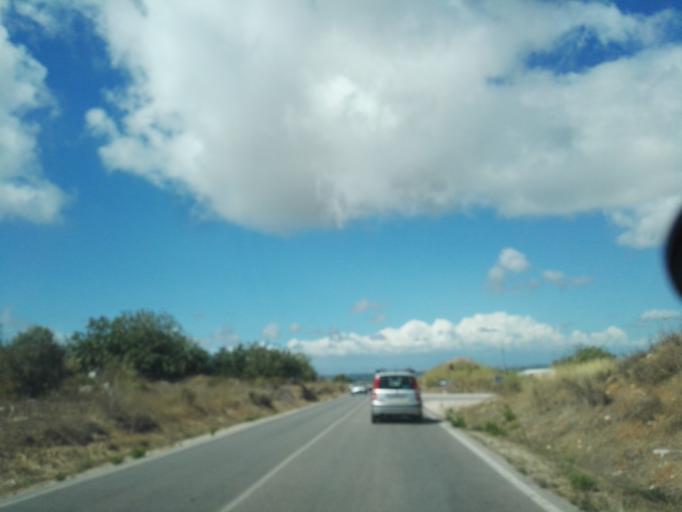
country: PT
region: Setubal
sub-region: Sesimbra
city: Sesimbra
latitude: 38.4590
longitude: -9.0938
